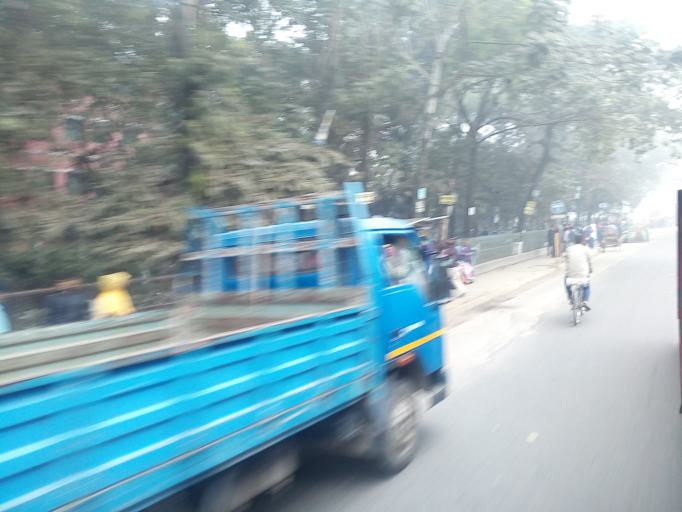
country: BD
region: Dhaka
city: Azimpur
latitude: 23.7772
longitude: 90.3804
